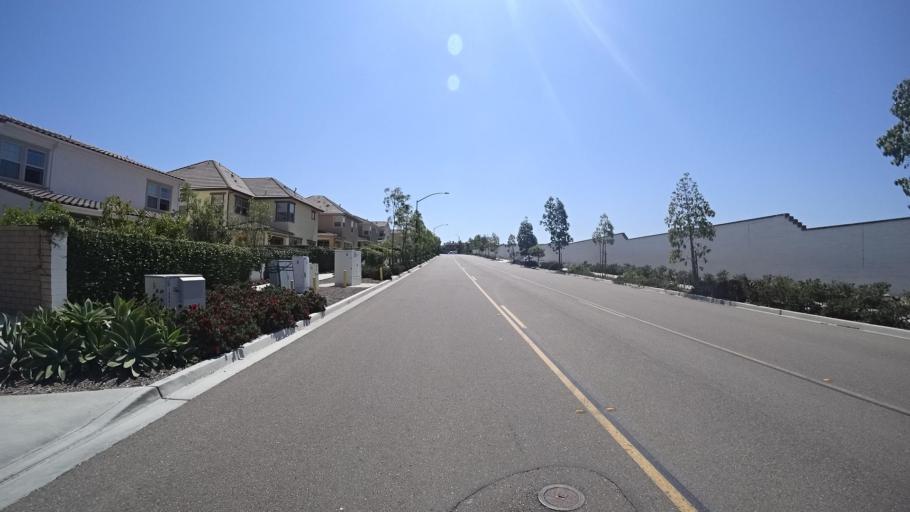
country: US
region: California
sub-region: San Diego County
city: Fairbanks Ranch
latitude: 32.9699
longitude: -117.1785
